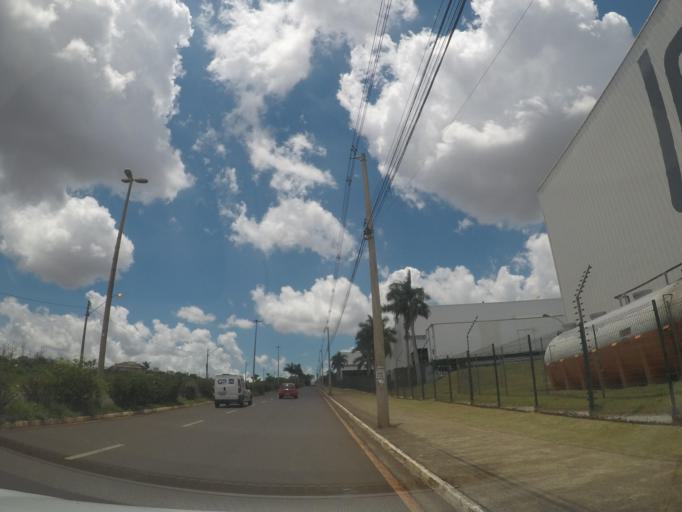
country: BR
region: Sao Paulo
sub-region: Hortolandia
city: Hortolandia
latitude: -22.8257
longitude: -47.2164
